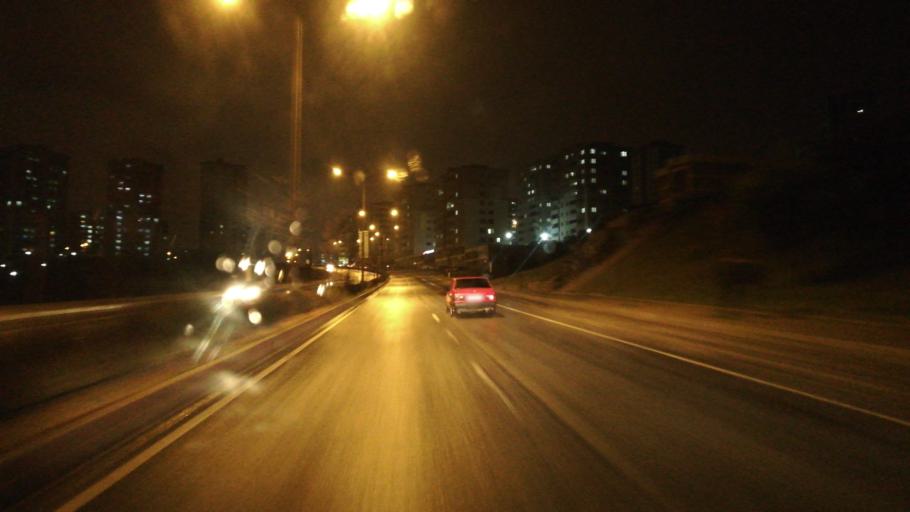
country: TR
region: Kahramanmaras
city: Kahramanmaras
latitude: 37.5788
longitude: 36.8607
